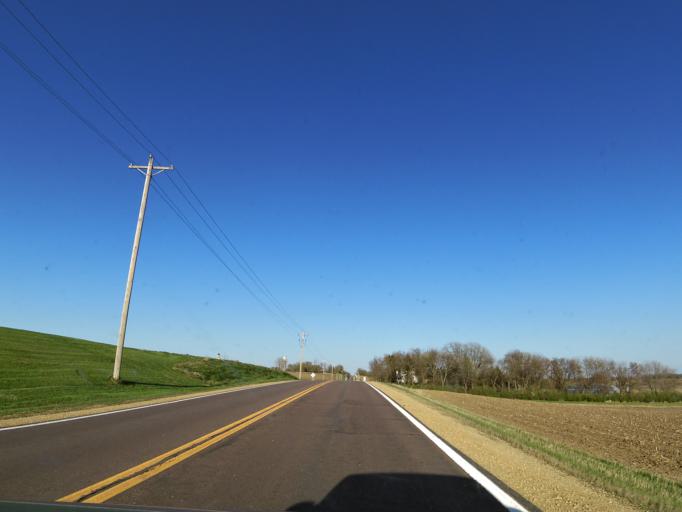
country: US
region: Minnesota
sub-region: Goodhue County
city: Cannon Falls
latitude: 44.6011
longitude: -92.9448
